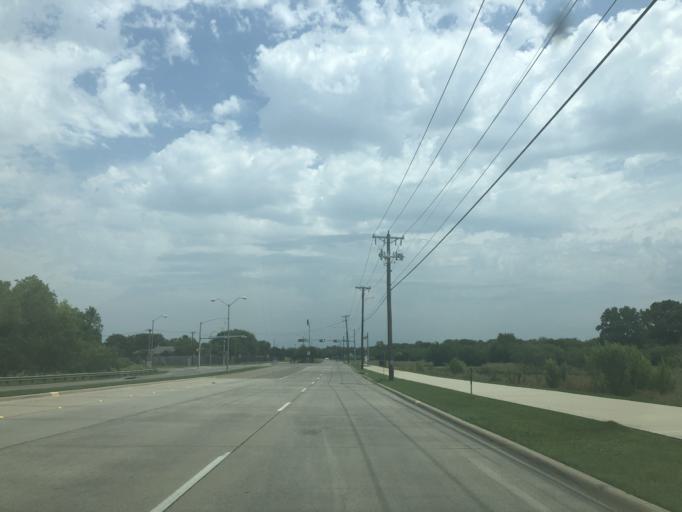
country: US
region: Texas
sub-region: Dallas County
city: Irving
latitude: 32.7817
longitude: -96.9599
